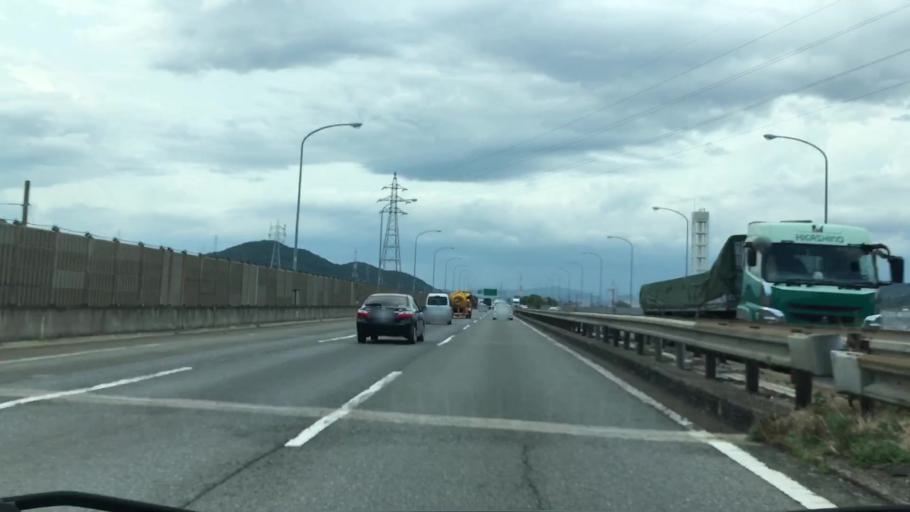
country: JP
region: Hyogo
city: Shirahamacho-usazakiminami
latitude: 34.7932
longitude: 134.7655
